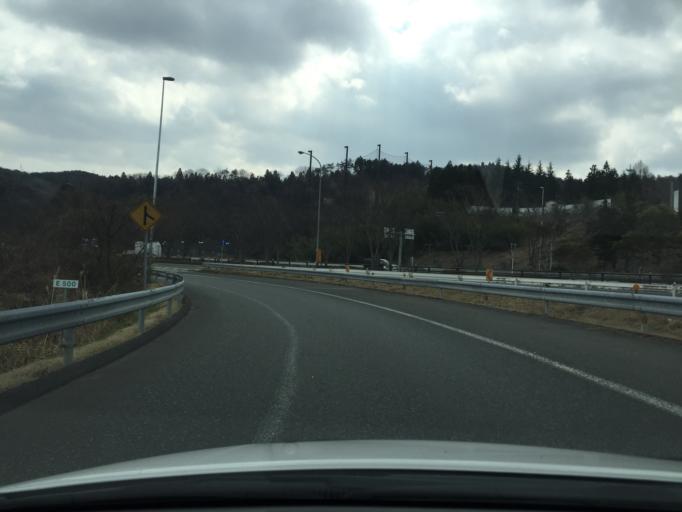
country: JP
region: Miyagi
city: Sendai
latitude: 38.2603
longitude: 140.8171
